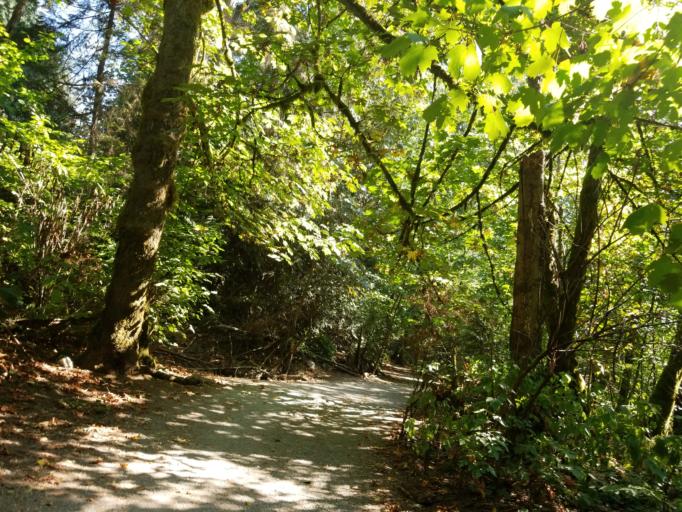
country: CA
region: British Columbia
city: West End
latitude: 49.2508
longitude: -123.2091
